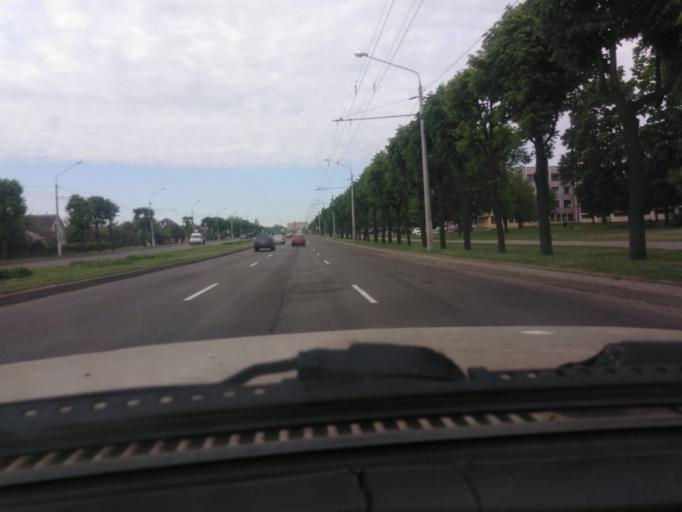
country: BY
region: Mogilev
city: Mahilyow
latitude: 53.9053
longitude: 30.3056
